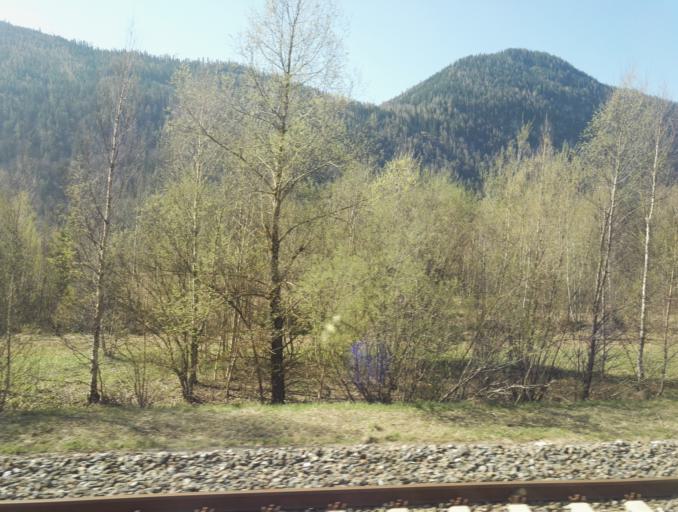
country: AT
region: Salzburg
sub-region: Politischer Bezirk Sankt Johann im Pongau
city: Forstau
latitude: 47.4044
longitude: 13.5660
